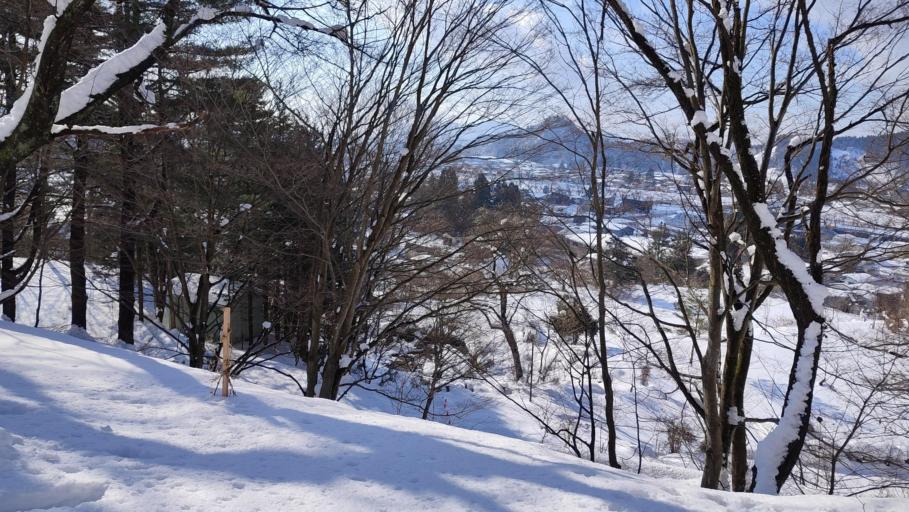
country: JP
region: Akita
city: Kakunodatemachi
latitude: 39.6050
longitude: 140.5619
